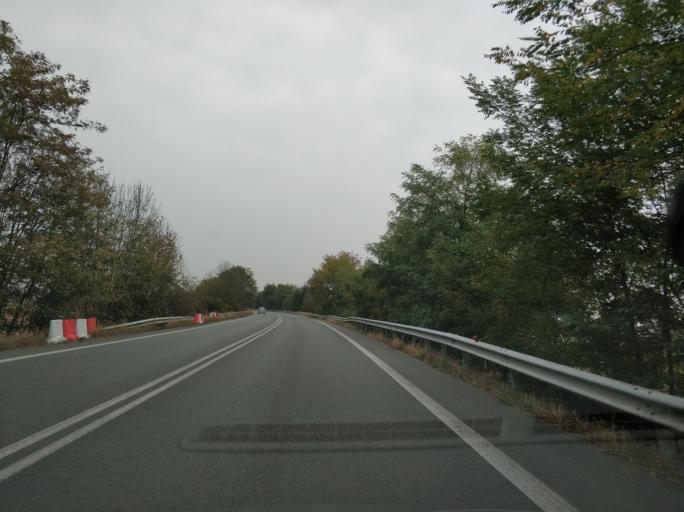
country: IT
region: Piedmont
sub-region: Provincia di Torino
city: Leini
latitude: 45.1975
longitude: 7.7030
